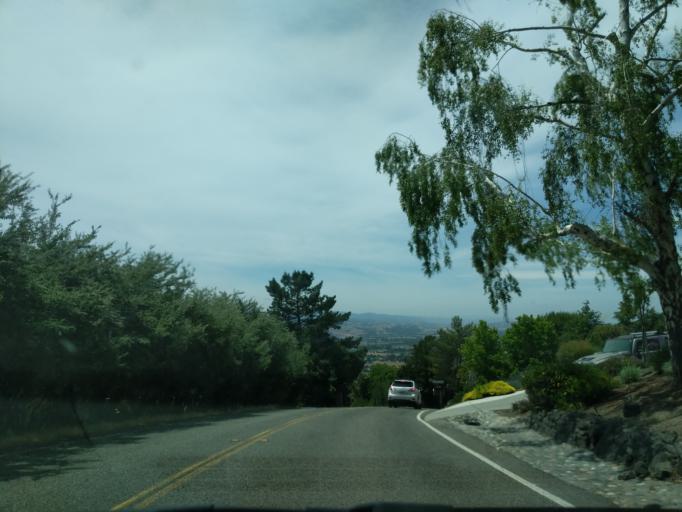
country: US
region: California
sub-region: Santa Clara County
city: San Martin
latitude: 37.1410
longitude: -121.5914
